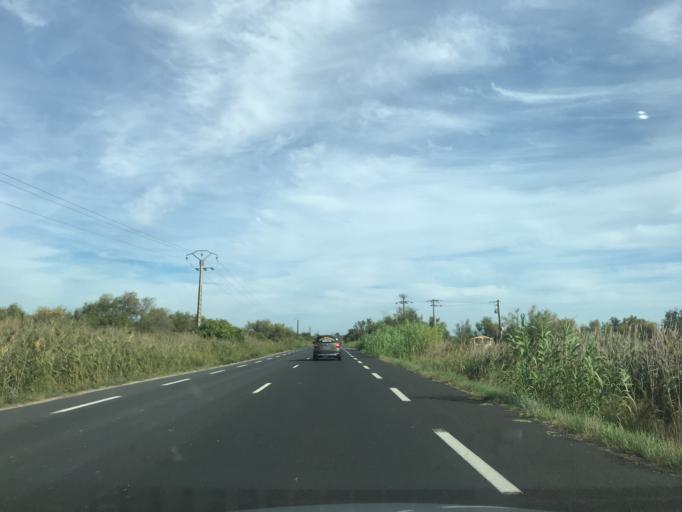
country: FR
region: Languedoc-Roussillon
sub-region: Departement du Gard
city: Aigues-Mortes
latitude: 43.5534
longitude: 4.3291
